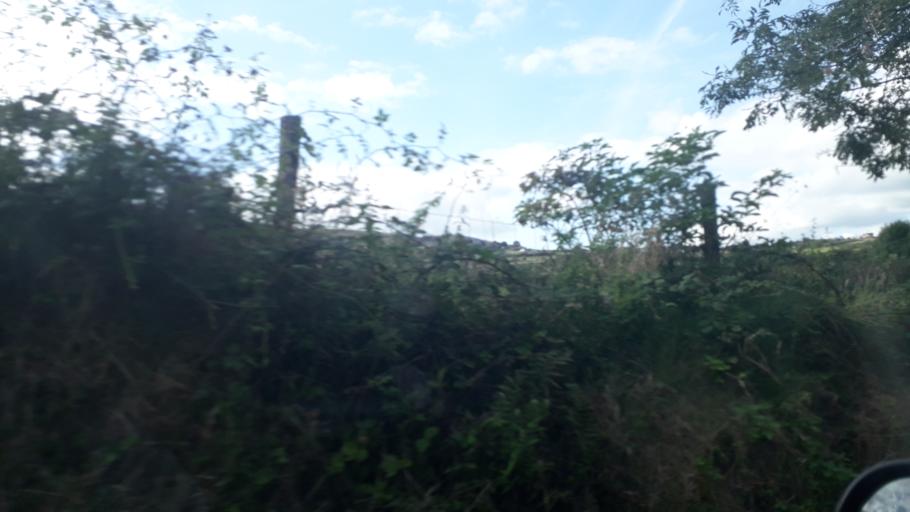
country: GB
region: Northern Ireland
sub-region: Down District
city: Warrenpoint
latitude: 54.0757
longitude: -6.2740
